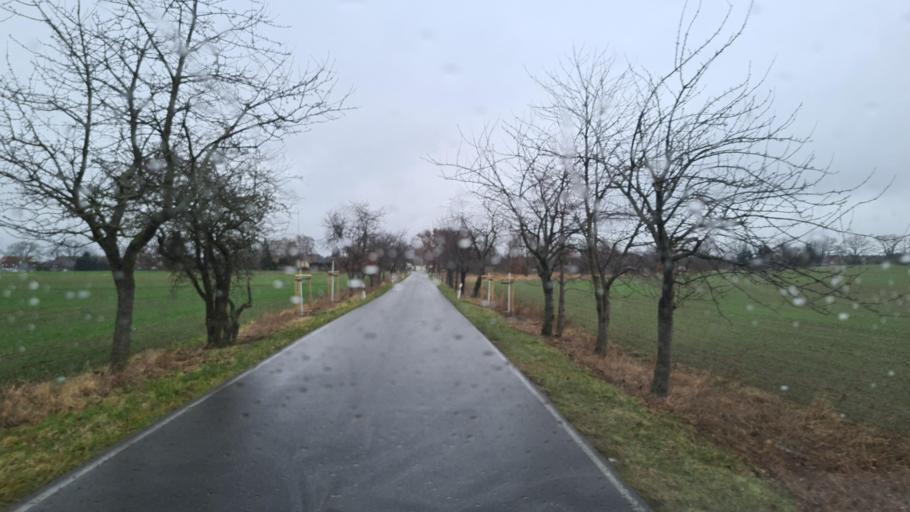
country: DE
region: Brandenburg
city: Gransee
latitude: 52.8946
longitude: 13.1999
